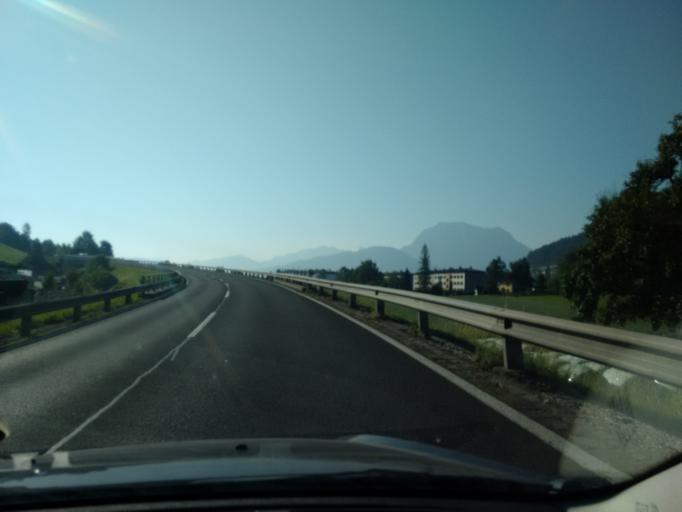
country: AT
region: Upper Austria
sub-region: Politischer Bezirk Gmunden
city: Altmunster
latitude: 47.9354
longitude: 13.7608
